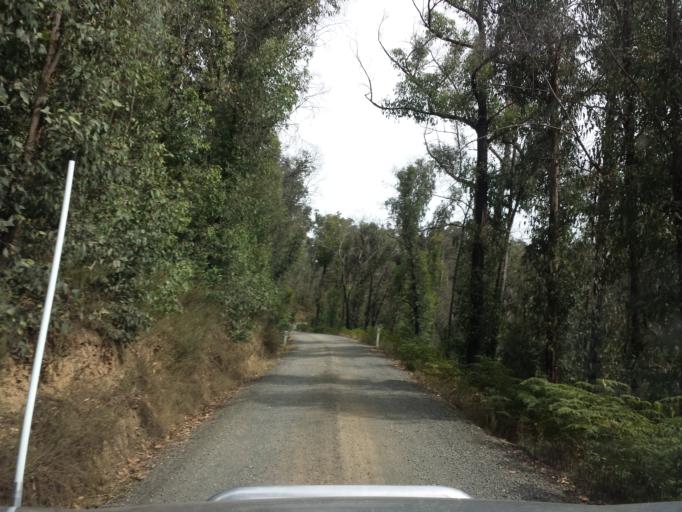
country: AU
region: Victoria
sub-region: Latrobe
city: Moe
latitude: -37.7895
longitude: 146.3840
